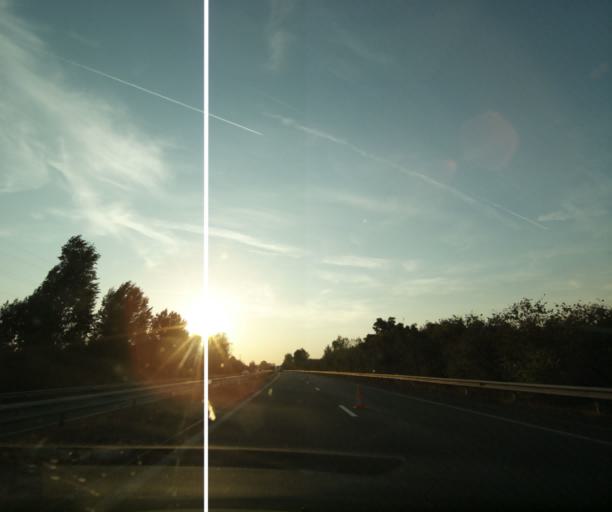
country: FR
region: Aquitaine
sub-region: Departement du Lot-et-Garonne
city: Sainte-Colombe-en-Bruilhois
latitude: 44.2110
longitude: 0.4725
